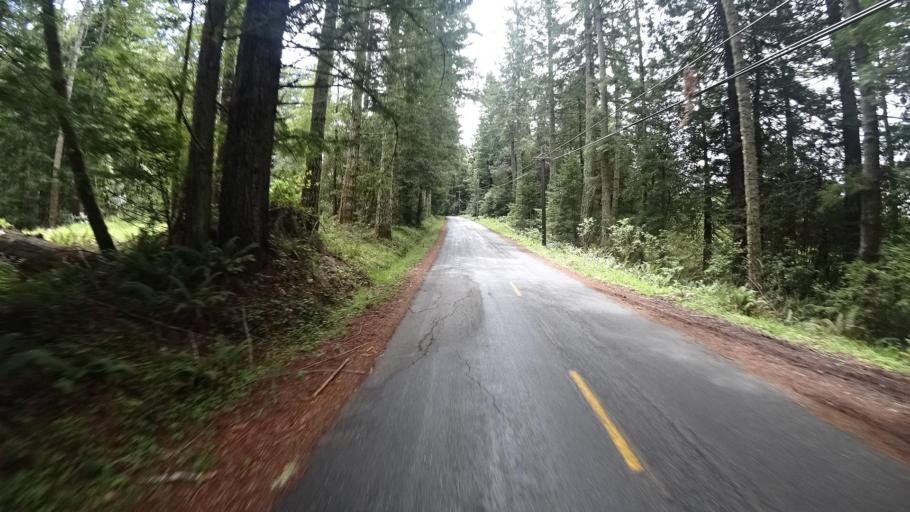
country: US
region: California
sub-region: Humboldt County
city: Bayside
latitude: 40.7793
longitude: -124.0080
